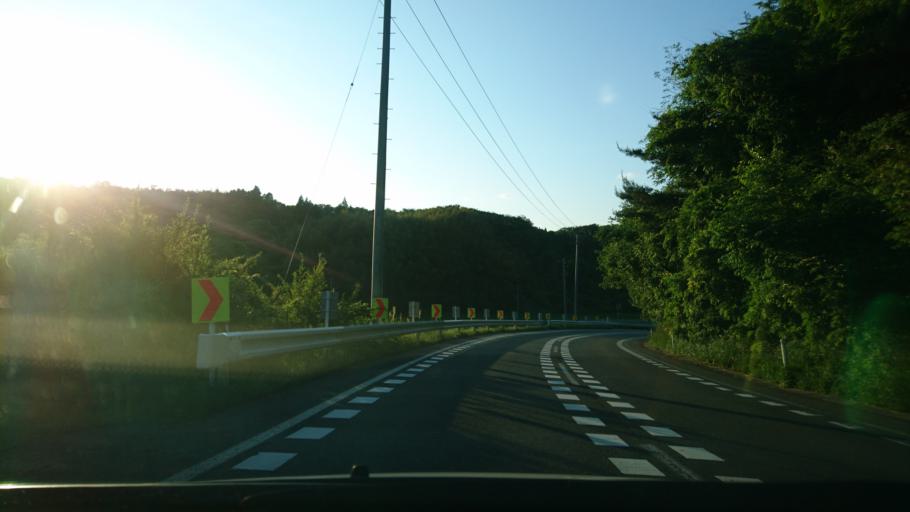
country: JP
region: Iwate
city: Ichinoseki
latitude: 38.8844
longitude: 141.1567
